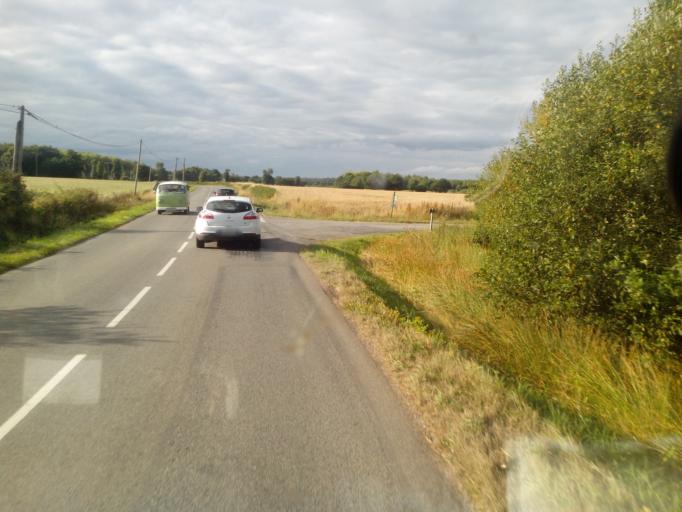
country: FR
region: Brittany
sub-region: Departement d'Ille-et-Vilaine
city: Paimpont
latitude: 48.0602
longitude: -2.1843
